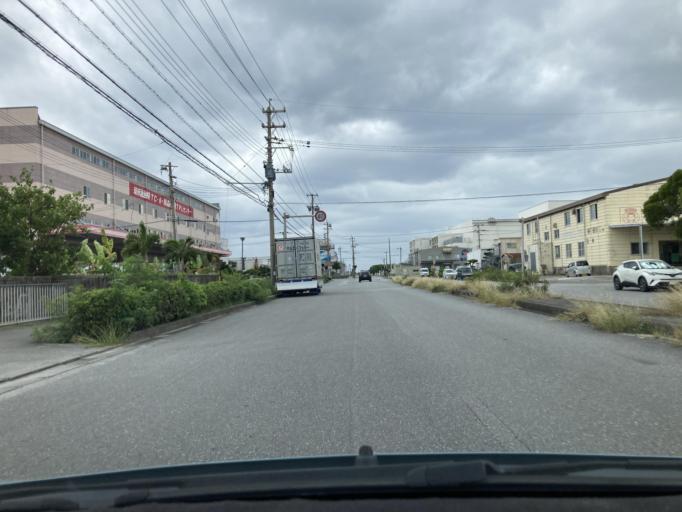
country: JP
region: Okinawa
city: Itoman
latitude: 26.1386
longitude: 127.6578
